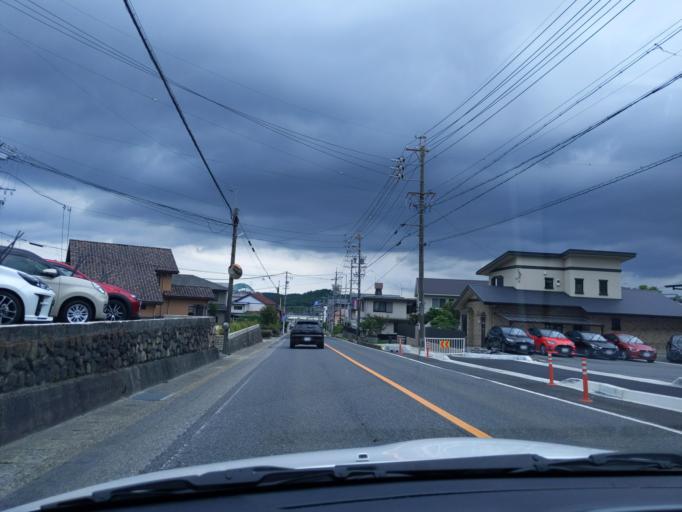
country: JP
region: Aichi
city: Seto
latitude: 35.2016
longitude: 137.1038
